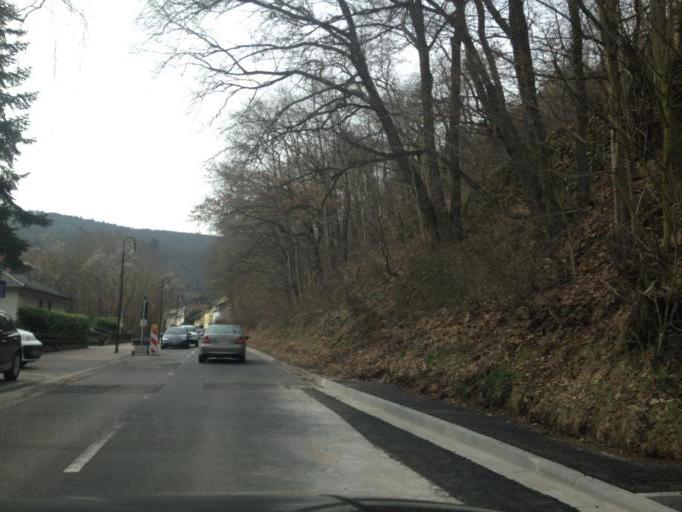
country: DE
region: Rheinland-Pfalz
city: Bad Duerkheim
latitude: 49.4605
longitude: 8.1308
